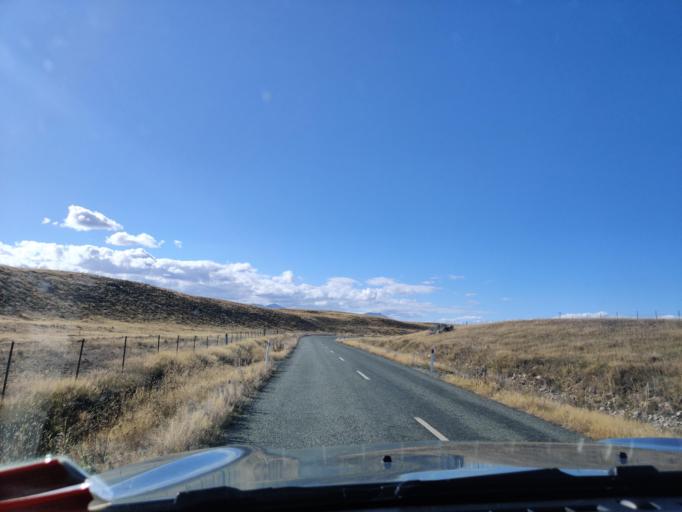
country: NZ
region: Canterbury
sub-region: Timaru District
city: Pleasant Point
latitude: -43.9921
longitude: 170.4496
